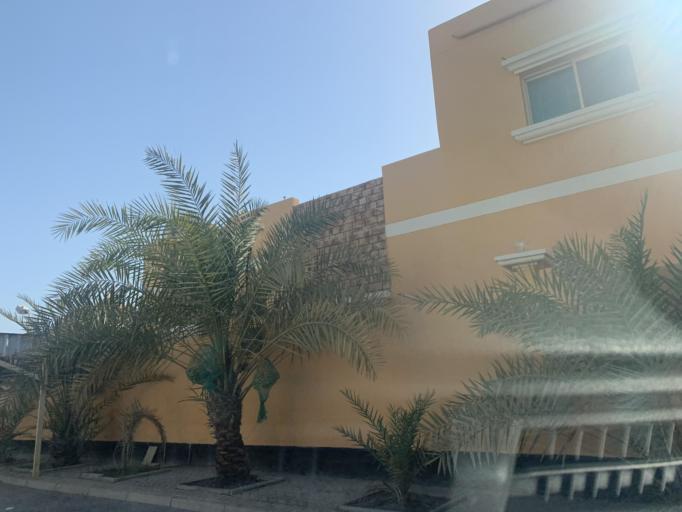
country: BH
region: Manama
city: Jidd Hafs
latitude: 26.2100
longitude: 50.4478
